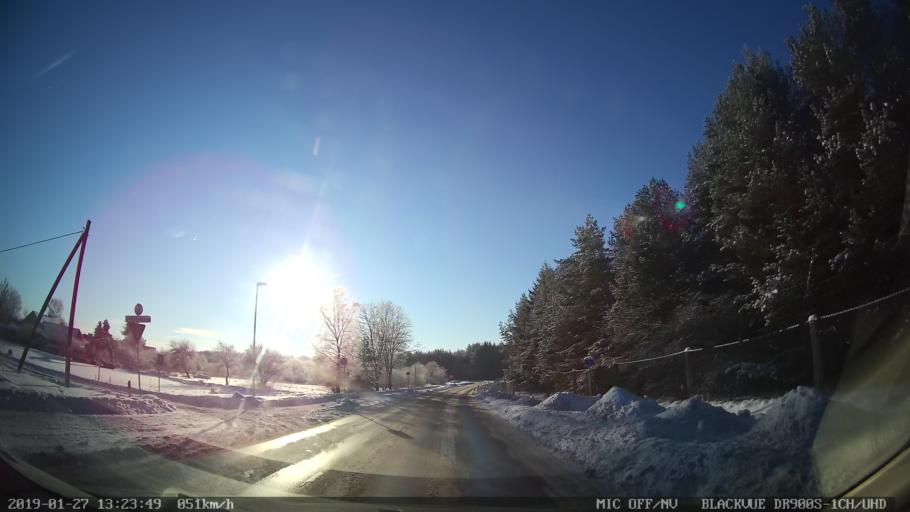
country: EE
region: Harju
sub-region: Tallinna linn
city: Tallinn
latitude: 59.4038
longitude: 24.7918
